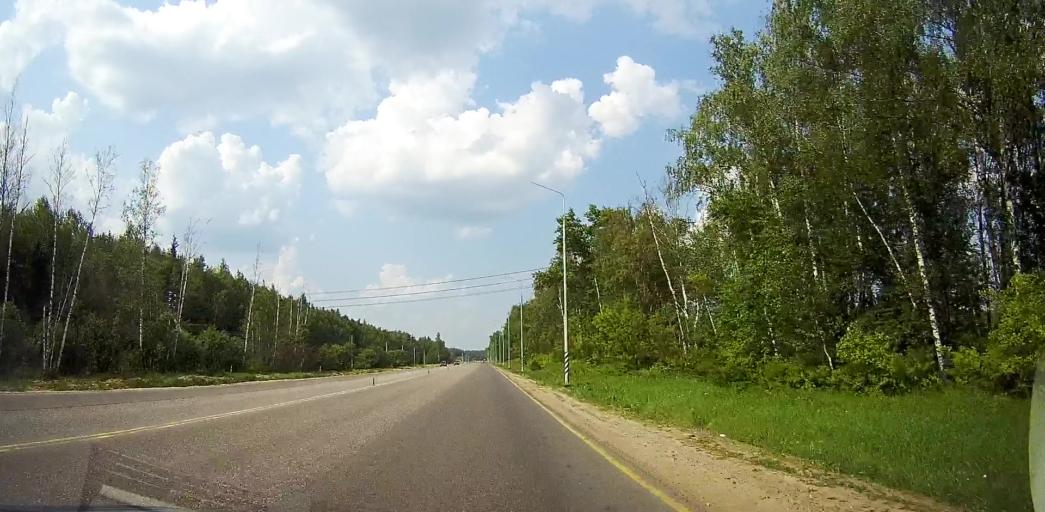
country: RU
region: Moskovskaya
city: Mikhnevo
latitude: 55.0648
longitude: 37.9536
